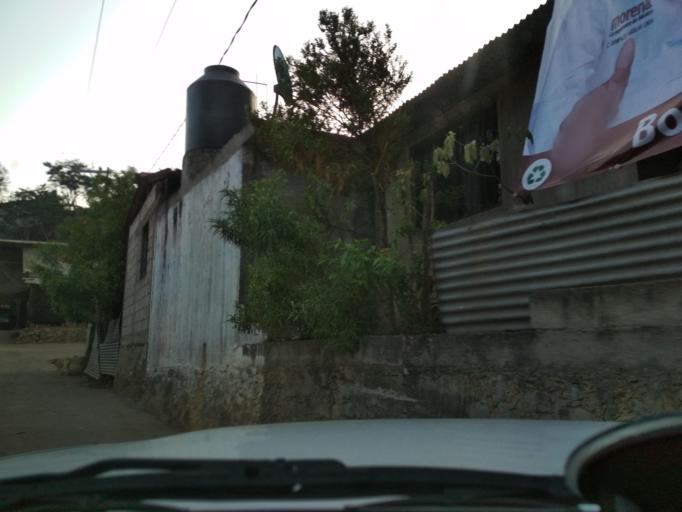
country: MX
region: Veracruz
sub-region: Nogales
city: Taza de Agua Ojo Zarco
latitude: 18.7711
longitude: -97.1933
